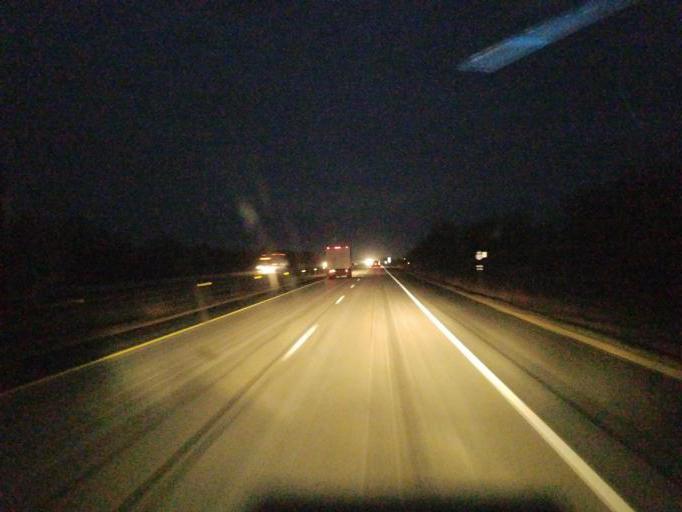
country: US
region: Iowa
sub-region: Guthrie County
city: Stuart
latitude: 41.4958
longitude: -94.4456
